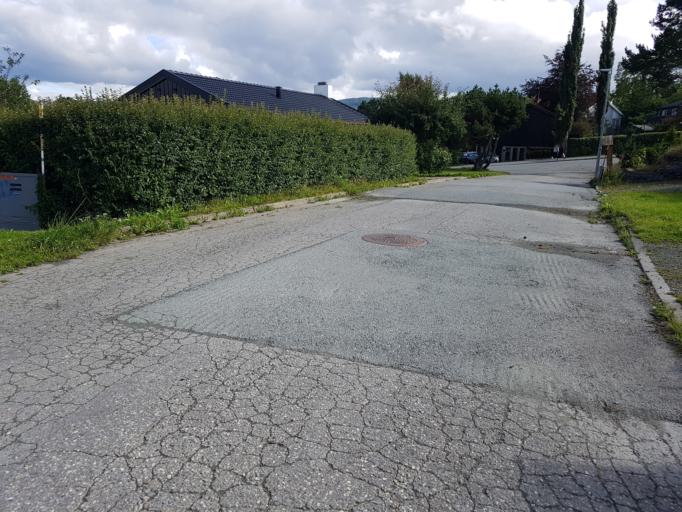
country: NO
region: Sor-Trondelag
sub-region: Trondheim
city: Trondheim
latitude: 63.4346
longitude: 10.4515
